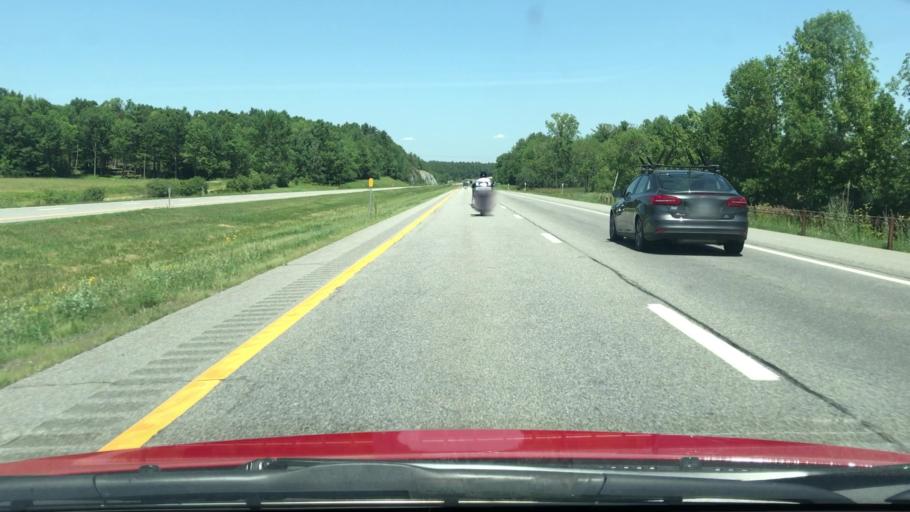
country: US
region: New York
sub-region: Essex County
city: Keeseville
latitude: 44.4688
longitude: -73.4862
